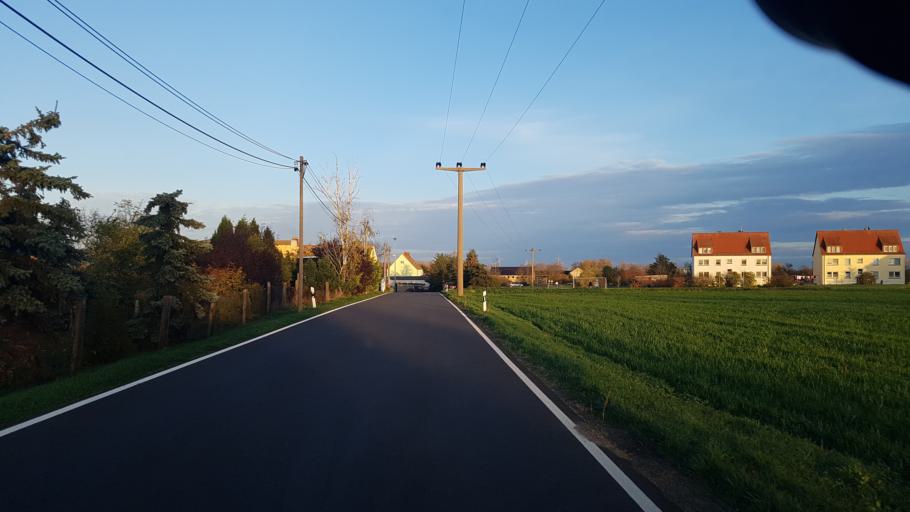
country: DE
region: Saxony
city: Belgern
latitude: 51.4632
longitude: 13.1622
